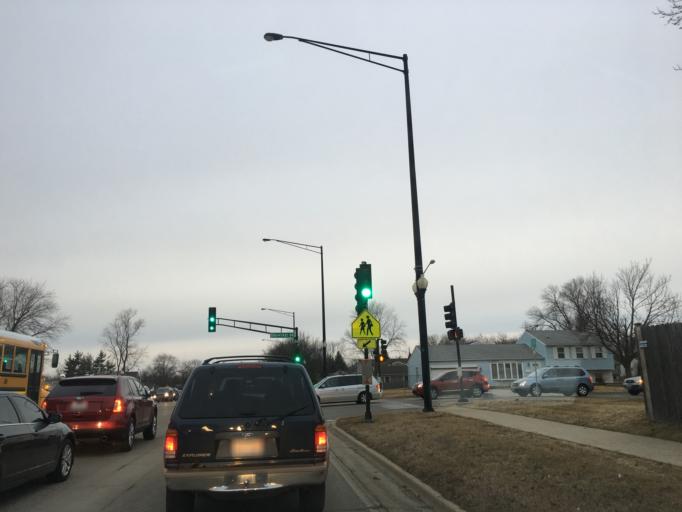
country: US
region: Illinois
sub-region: Cook County
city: Schaumburg
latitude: 42.0263
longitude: -88.1095
